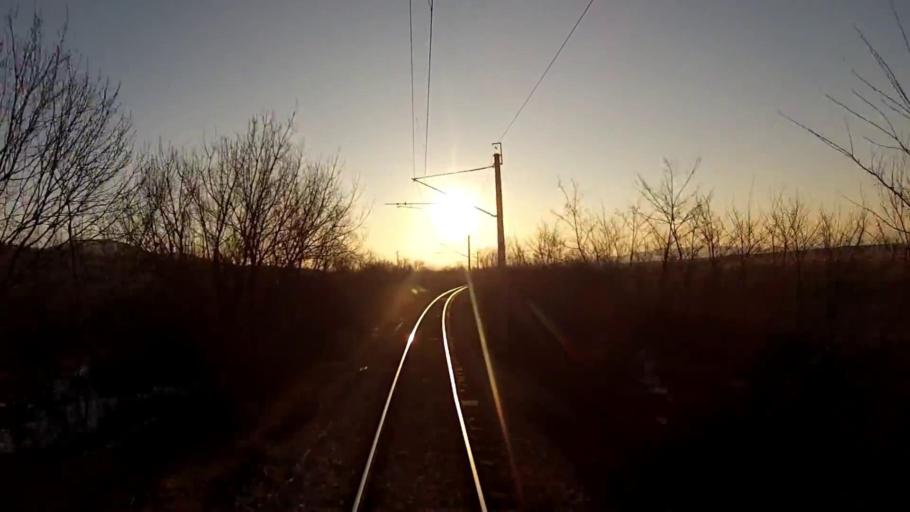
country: BG
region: Sofiya
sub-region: Obshtina Dragoman
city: Dragoman
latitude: 42.8943
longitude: 22.9694
